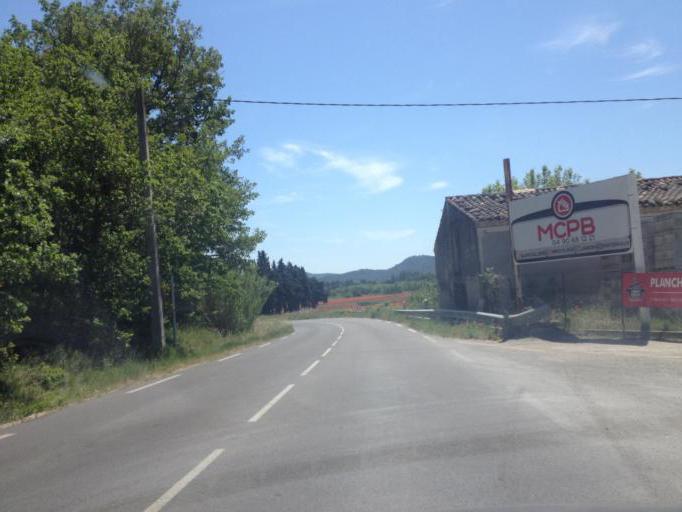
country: FR
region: Provence-Alpes-Cote d'Azur
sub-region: Departement du Vaucluse
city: Lauris
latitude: 43.7424
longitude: 5.3445
